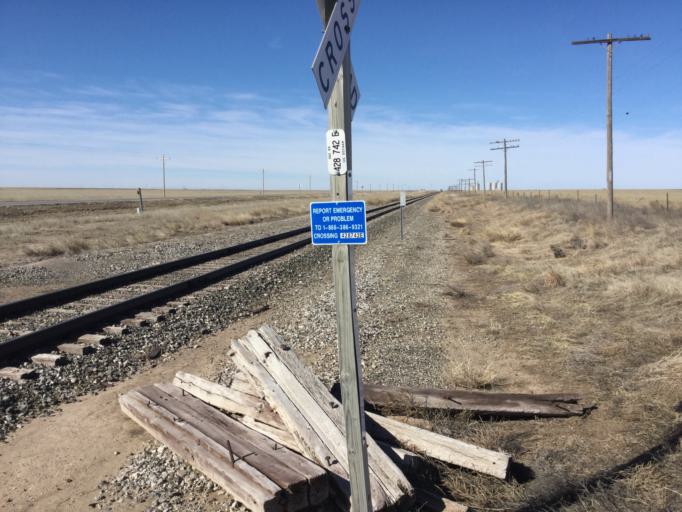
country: US
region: Kansas
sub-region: Wichita County
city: Leoti
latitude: 38.4806
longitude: -101.5034
